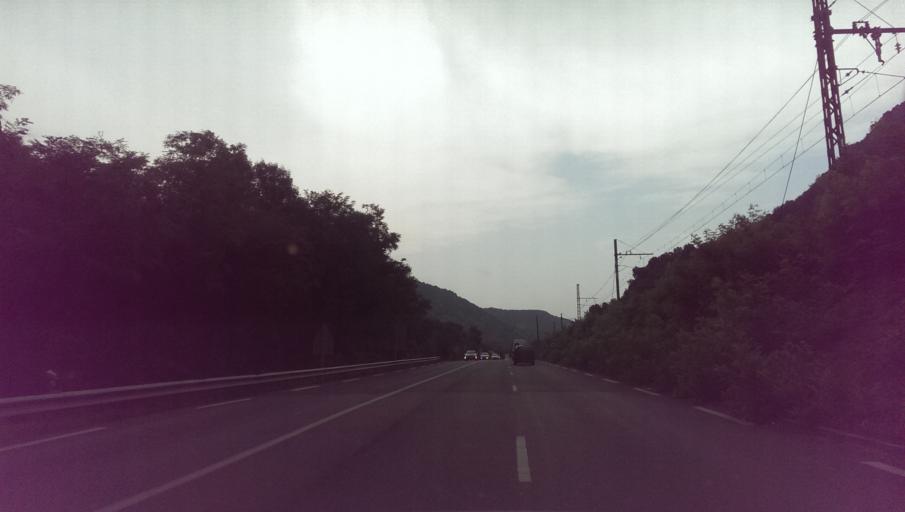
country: FR
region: Languedoc-Roussillon
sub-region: Departement des Pyrenees-Orientales
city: Ria-Sirach
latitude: 42.5975
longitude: 2.3780
